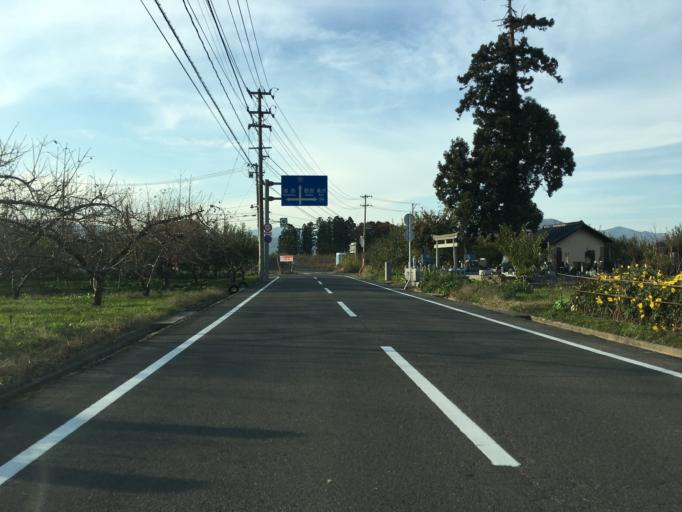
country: JP
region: Fukushima
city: Fukushima-shi
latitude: 37.8072
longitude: 140.4605
